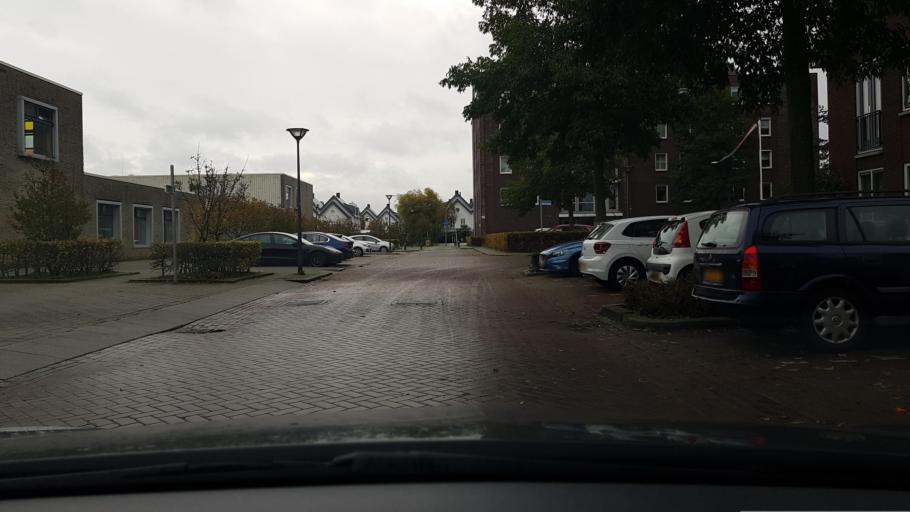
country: NL
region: North Holland
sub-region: Gemeente Bloemendaal
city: Bennebroek
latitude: 52.3057
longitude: 4.6385
